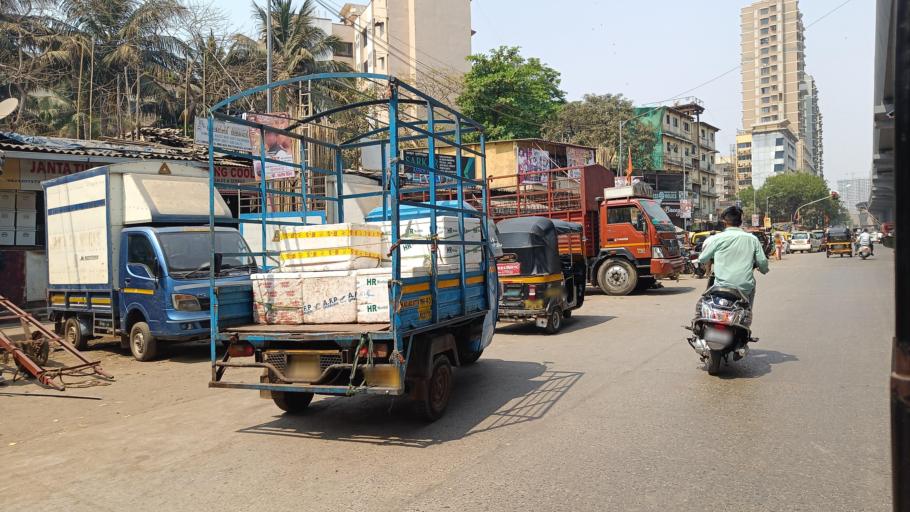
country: IN
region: Maharashtra
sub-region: Mumbai Suburban
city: Powai
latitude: 19.1477
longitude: 72.8364
